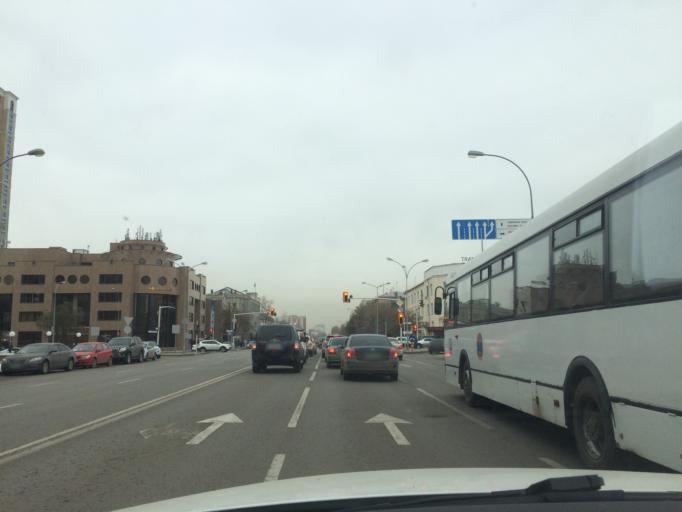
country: KZ
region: Astana Qalasy
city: Astana
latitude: 51.1660
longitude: 71.4140
